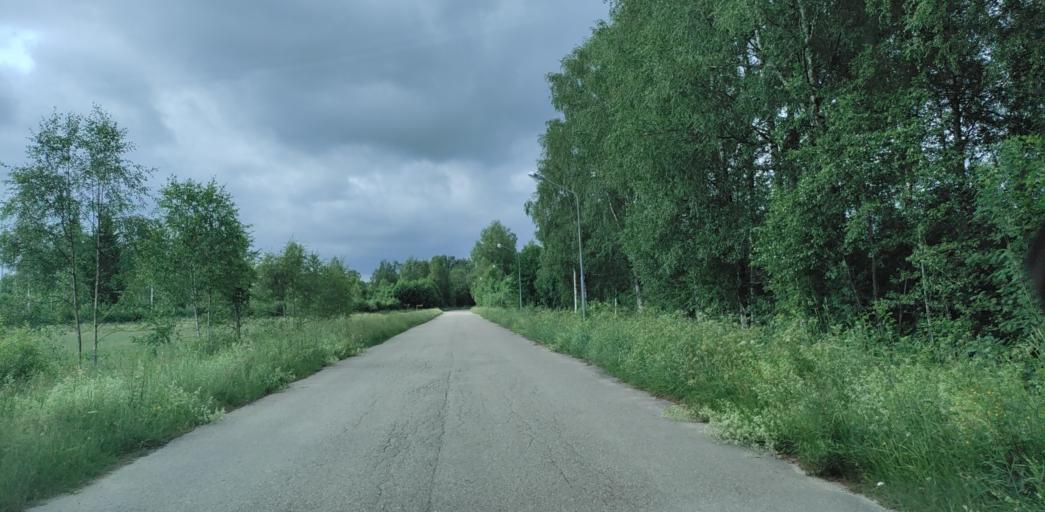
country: SE
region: Vaermland
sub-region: Hagfors Kommun
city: Hagfors
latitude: 60.0658
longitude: 13.5694
